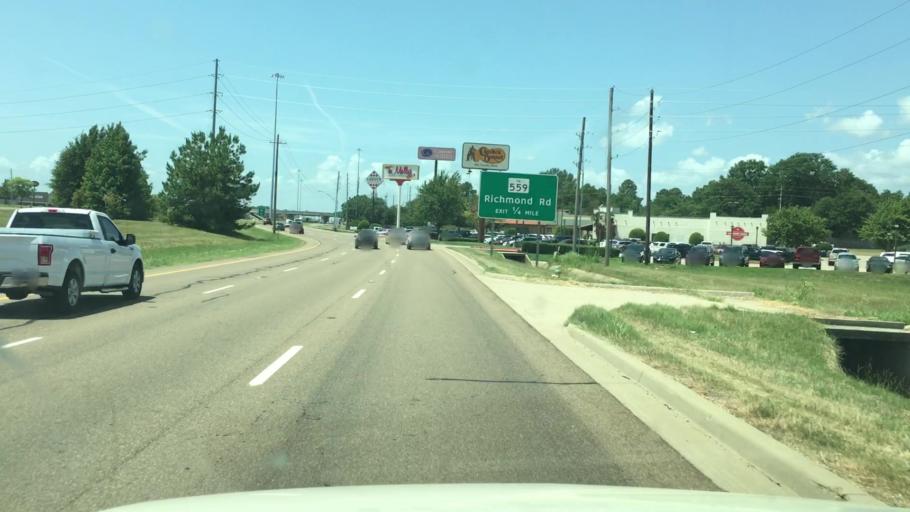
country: US
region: Texas
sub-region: Bowie County
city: Wake Village
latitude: 33.4602
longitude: -94.0800
